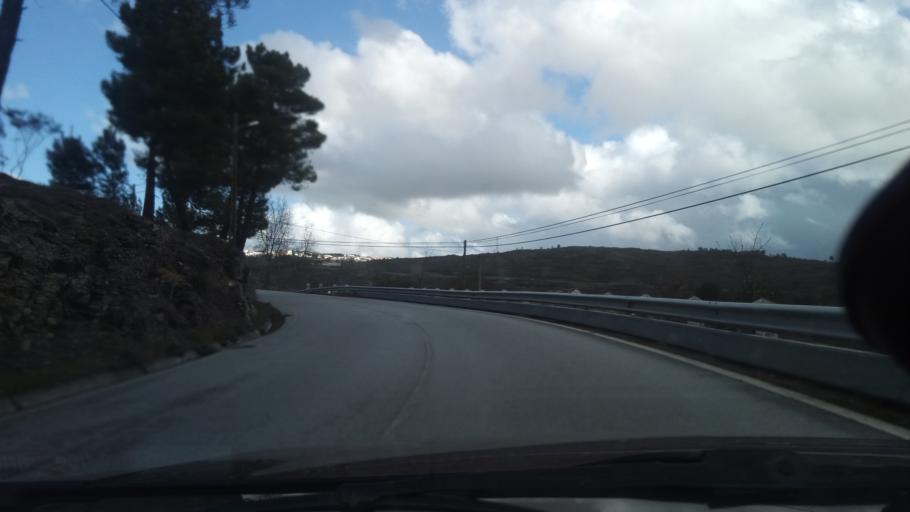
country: PT
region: Guarda
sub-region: Guarda
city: Guarda
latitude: 40.5381
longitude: -7.3117
